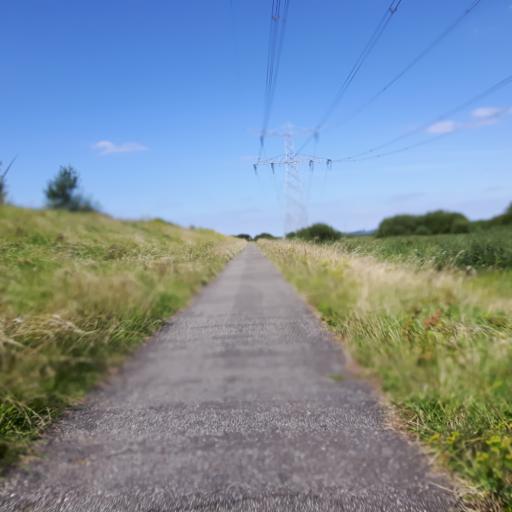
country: NL
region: North Brabant
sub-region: Gemeente Bergen op Zoom
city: Bergen op Zoom
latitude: 51.4529
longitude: 4.2384
